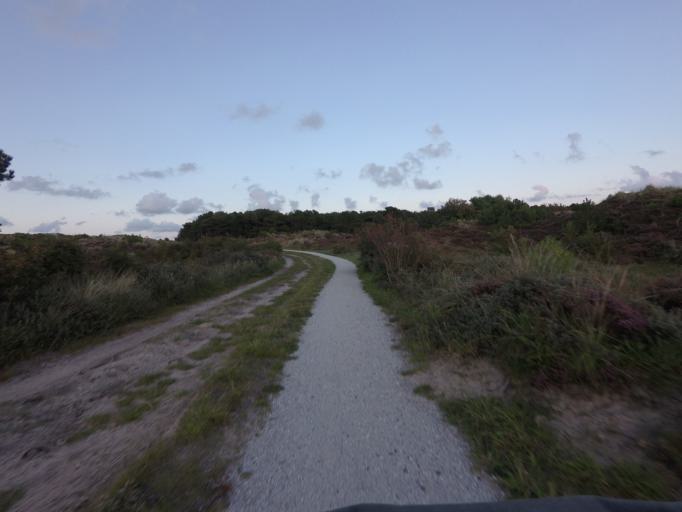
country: NL
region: Friesland
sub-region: Gemeente Terschelling
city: West-Terschelling
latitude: 53.3615
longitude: 5.2058
